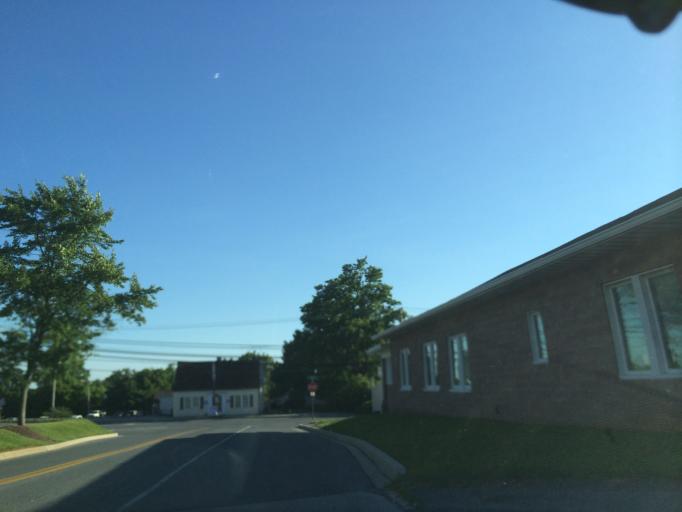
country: US
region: Maryland
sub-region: Carroll County
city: Westminster
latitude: 39.5628
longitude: -76.9805
